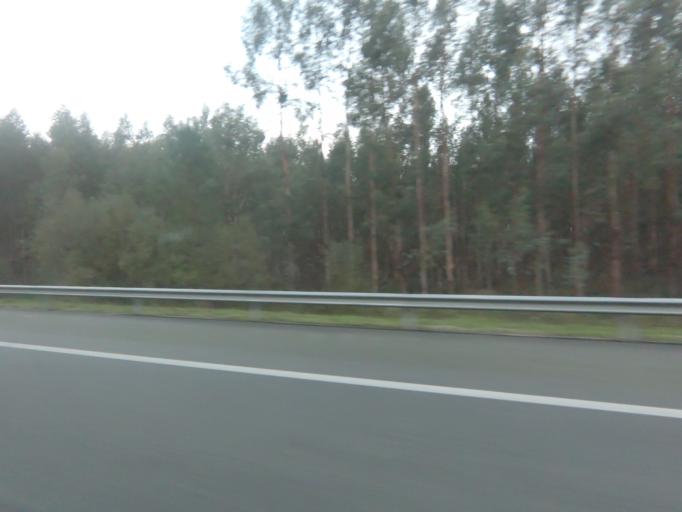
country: PT
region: Braga
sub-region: Barcelos
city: Galegos
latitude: 41.6282
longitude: -8.5604
